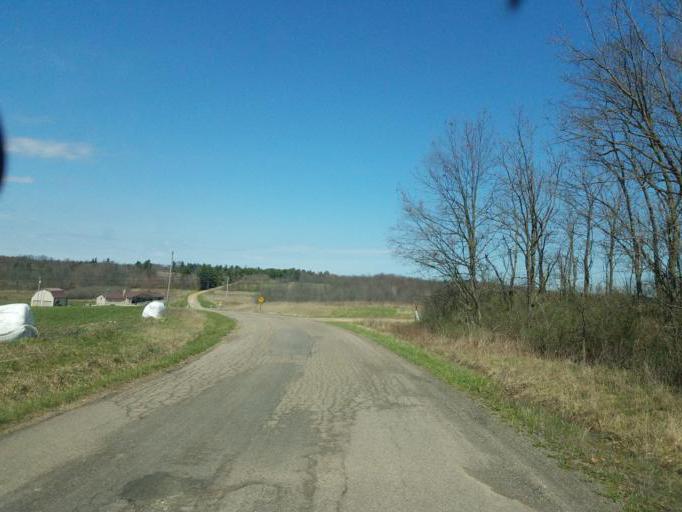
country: US
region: Ohio
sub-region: Knox County
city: Oak Hill
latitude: 40.3466
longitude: -82.1901
